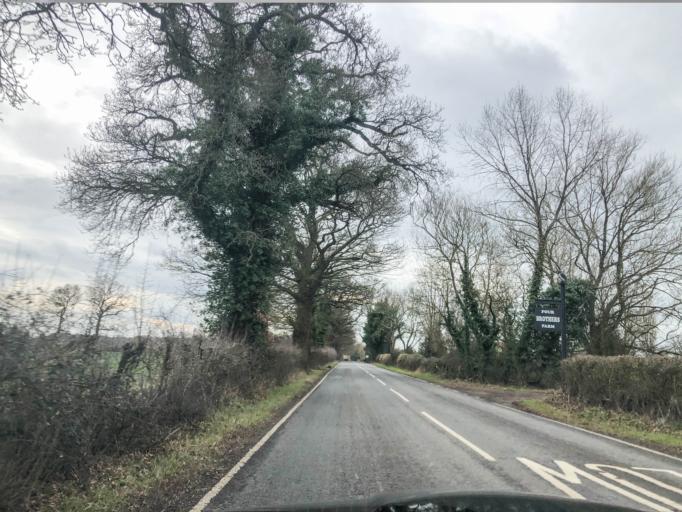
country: GB
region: England
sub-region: Warwickshire
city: Wroxall
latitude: 52.3226
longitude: -1.6701
